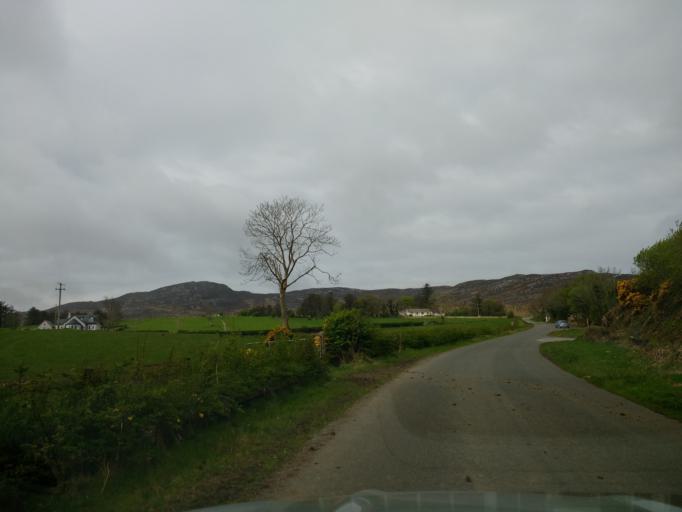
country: IE
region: Ulster
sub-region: County Donegal
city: Buncrana
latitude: 55.1691
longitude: -7.5785
